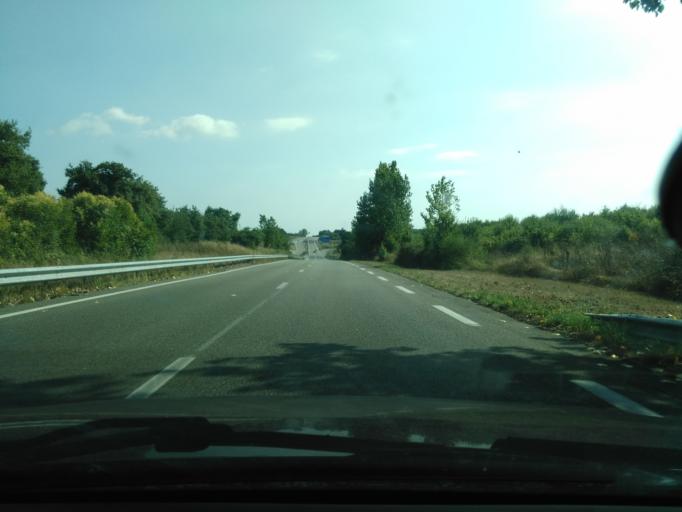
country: FR
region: Pays de la Loire
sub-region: Departement de la Vendee
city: Aubigny
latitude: 46.6307
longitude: -1.4404
